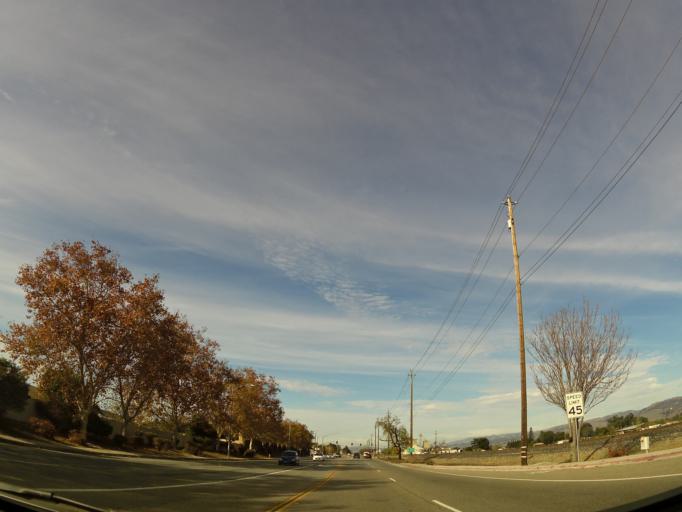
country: US
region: California
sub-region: Santa Clara County
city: Gilroy
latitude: 37.0298
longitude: -121.5801
